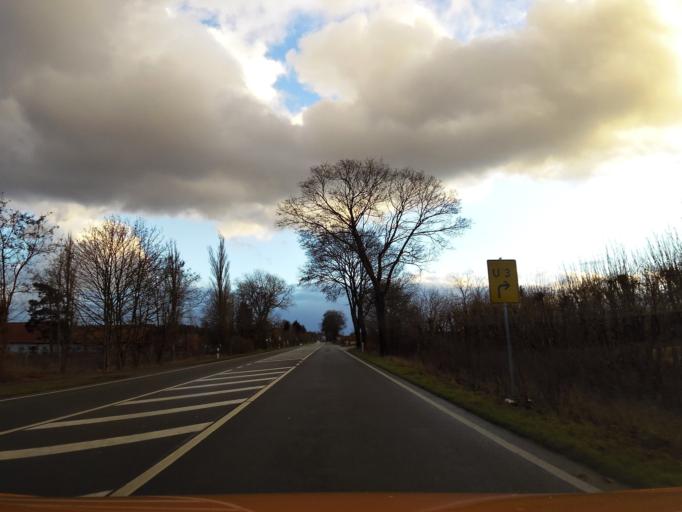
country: DE
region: Lower Saxony
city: Didderse
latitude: 52.3827
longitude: 10.3782
